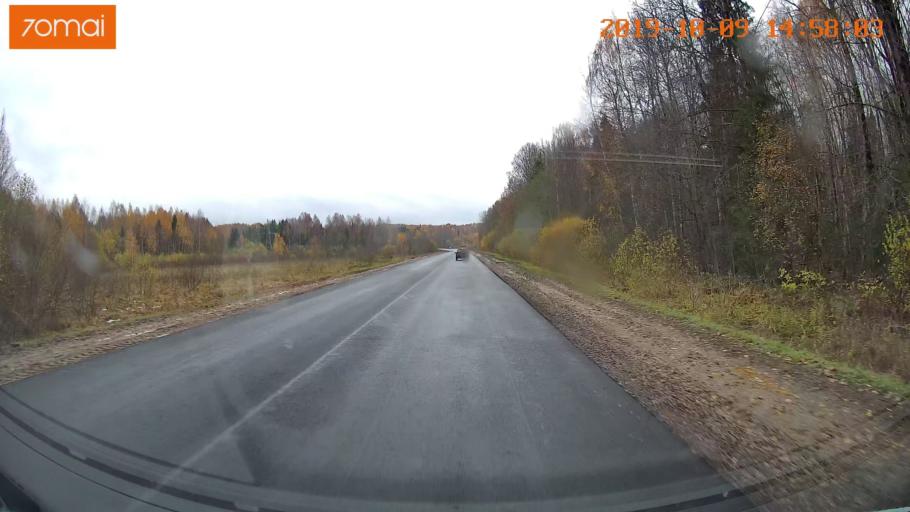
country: RU
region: Kostroma
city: Chistyye Bory
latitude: 58.3310
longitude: 41.6533
